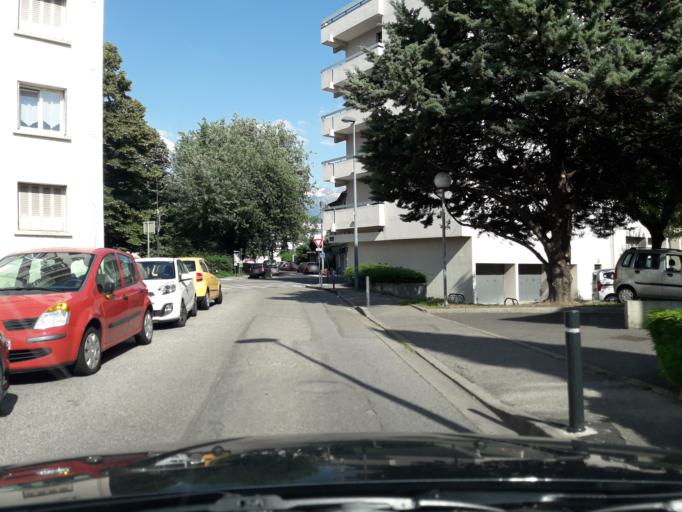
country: FR
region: Rhone-Alpes
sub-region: Departement de l'Isere
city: La Tronche
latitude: 45.1830
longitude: 5.7436
